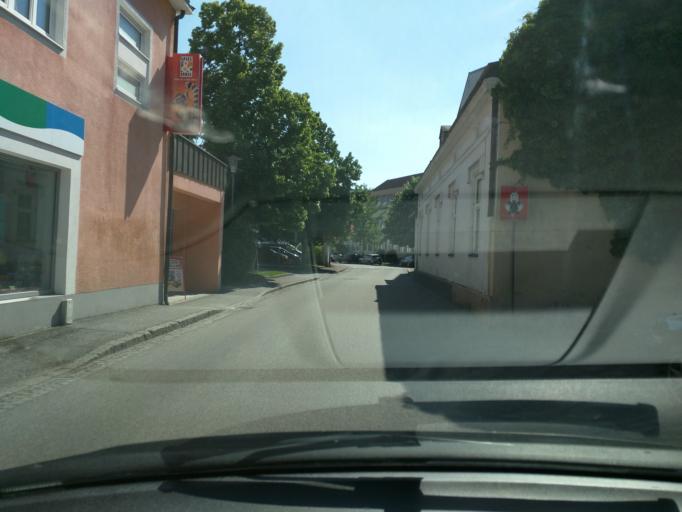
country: AT
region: Lower Austria
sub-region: Politischer Bezirk Melk
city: Ybbs an der Donau
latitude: 48.1786
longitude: 15.0836
